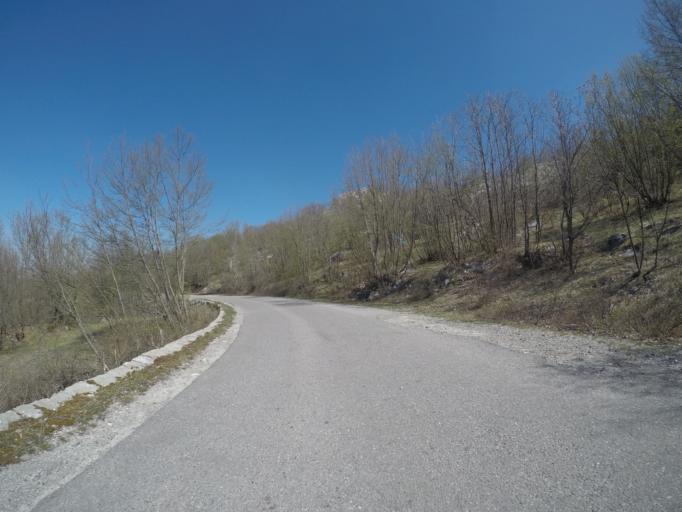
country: ME
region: Cetinje
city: Cetinje
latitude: 42.4464
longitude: 18.8735
